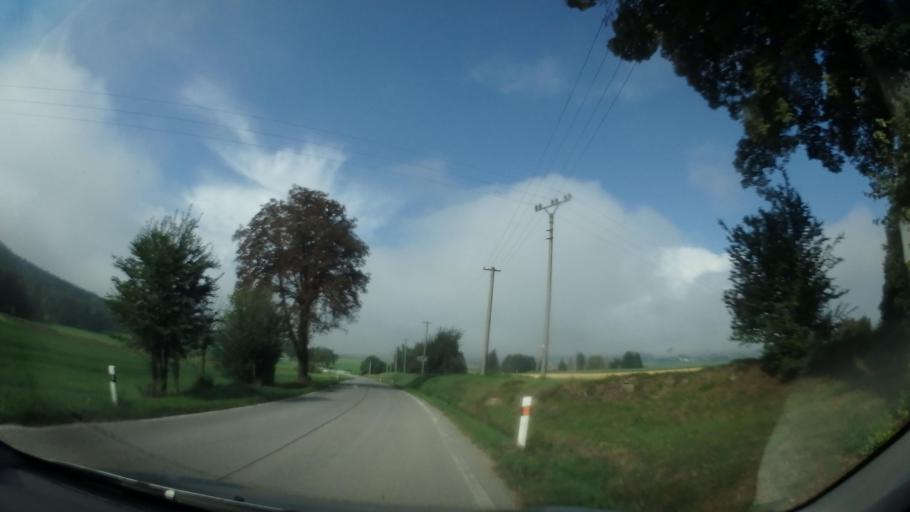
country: CZ
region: Jihocesky
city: Katovice
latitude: 49.2632
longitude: 13.7921
